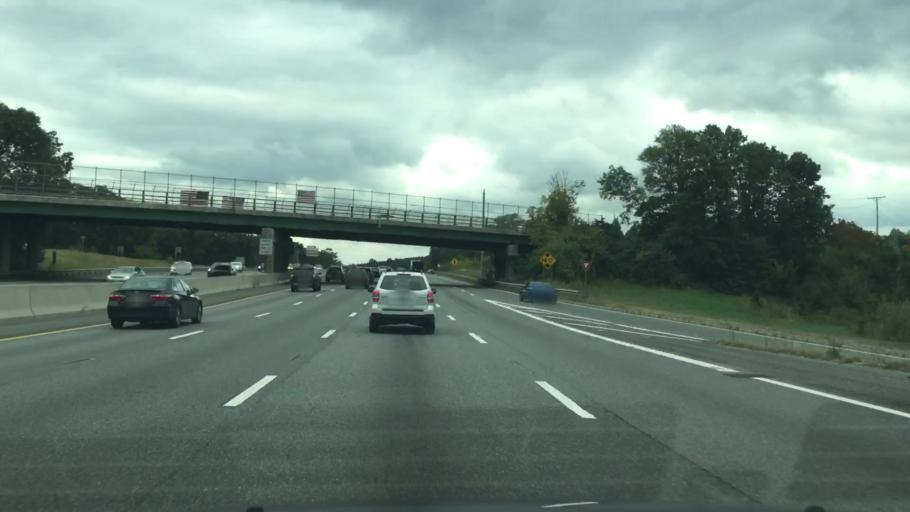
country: US
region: Massachusetts
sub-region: Middlesex County
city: Waltham
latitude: 42.3783
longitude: -71.2658
